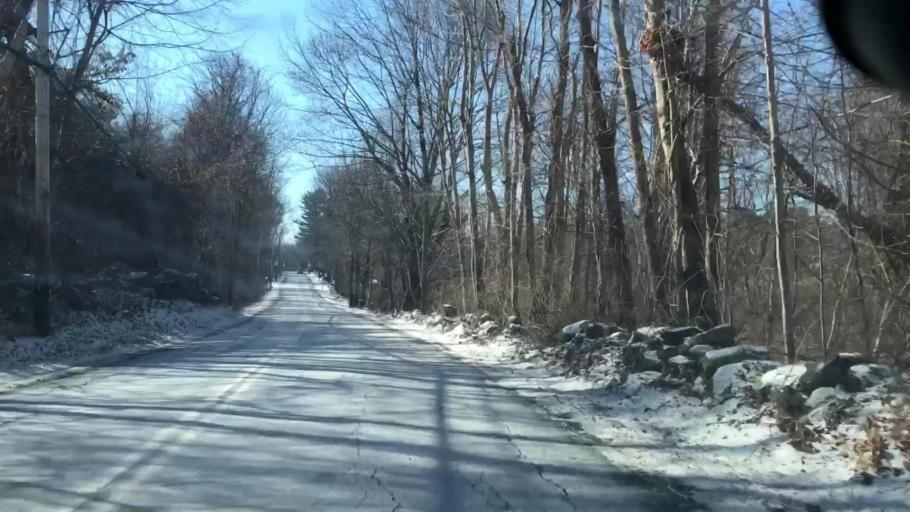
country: US
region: New York
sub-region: Putnam County
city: Mahopac
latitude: 41.3821
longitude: -73.7066
